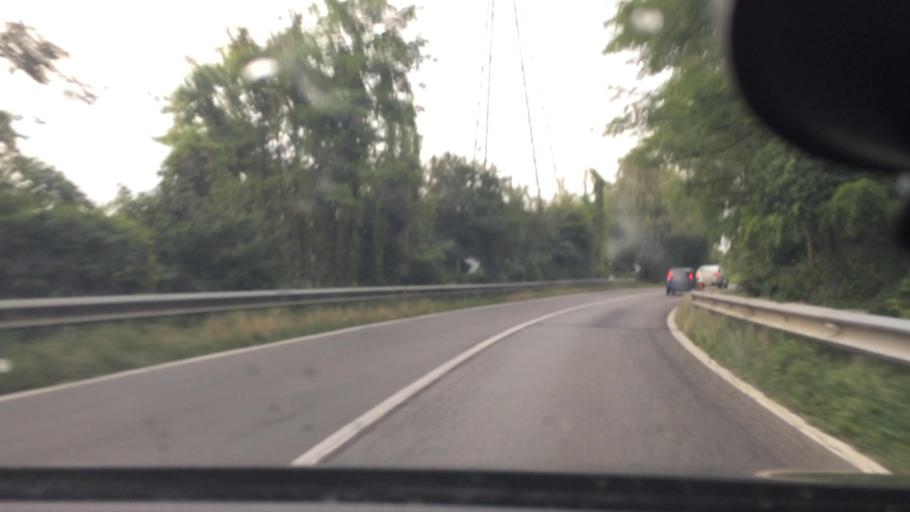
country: IT
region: Lombardy
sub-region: Provincia di Monza e Brianza
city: Villaggio del Sole
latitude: 45.6353
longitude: 9.1029
